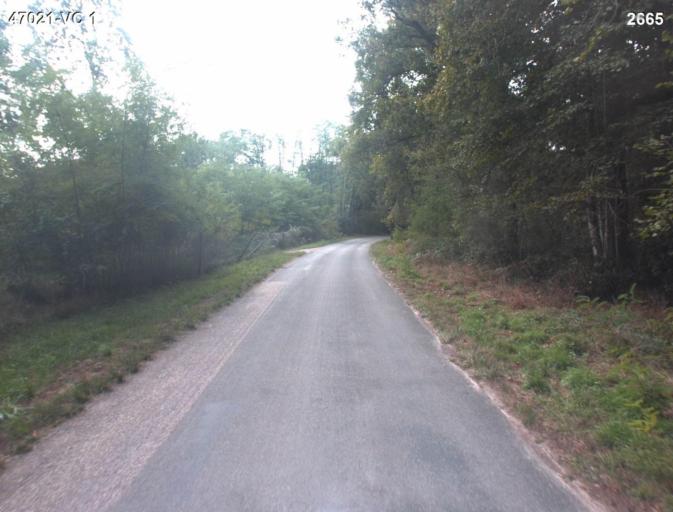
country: FR
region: Aquitaine
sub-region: Departement du Lot-et-Garonne
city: Barbaste
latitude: 44.1440
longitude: 0.2952
